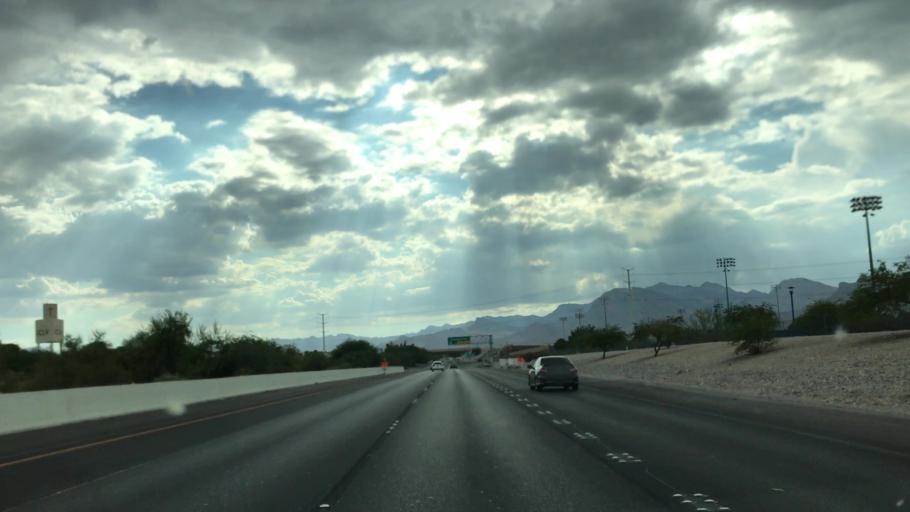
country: US
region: Nevada
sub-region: Clark County
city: Spring Valley
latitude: 36.1782
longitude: -115.2682
